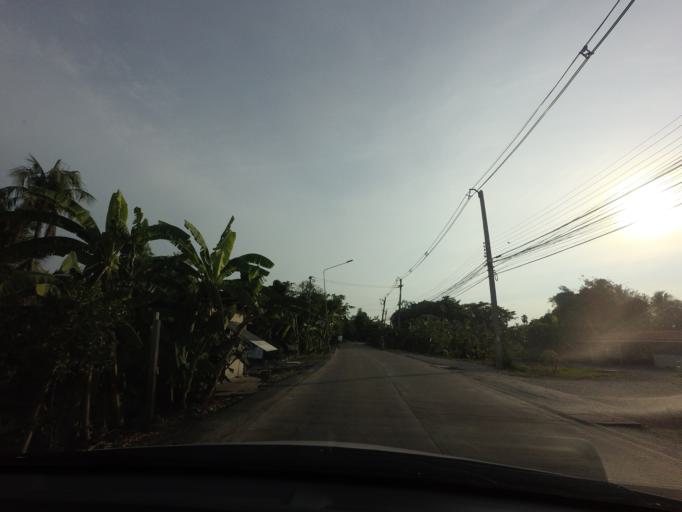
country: TH
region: Pathum Thani
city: Pathum Thani
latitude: 14.0397
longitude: 100.5501
